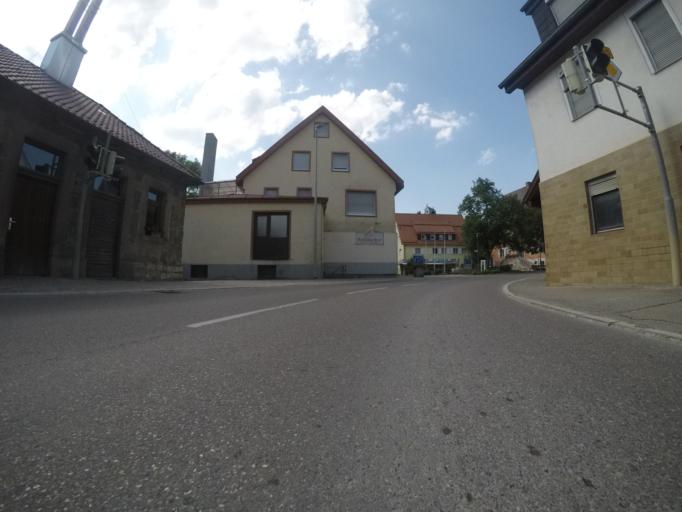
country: DE
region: Baden-Wuerttemberg
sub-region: Tuebingen Region
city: Grabenstetten
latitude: 48.5502
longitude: 9.4707
